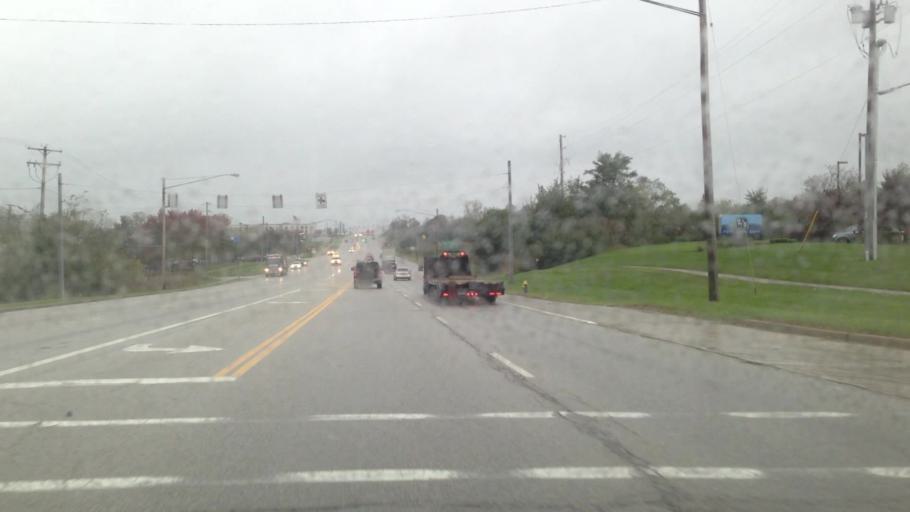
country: US
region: Ohio
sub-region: Portage County
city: Streetsboro
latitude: 41.2448
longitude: -81.3566
